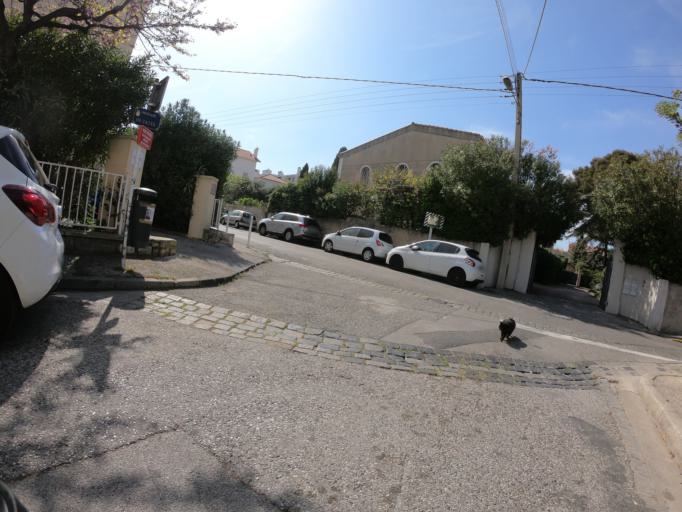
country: FR
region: Provence-Alpes-Cote d'Azur
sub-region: Departement du Var
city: Toulon
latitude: 43.1063
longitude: 5.9338
